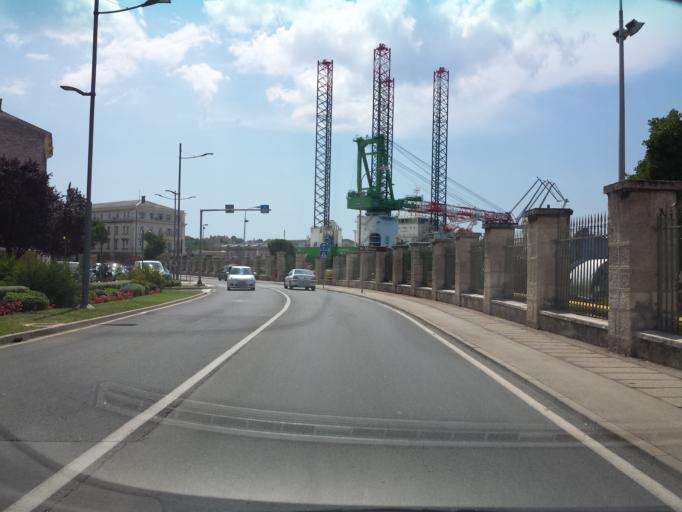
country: HR
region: Istarska
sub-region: Grad Pula
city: Pula
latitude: 44.8702
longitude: 13.8414
